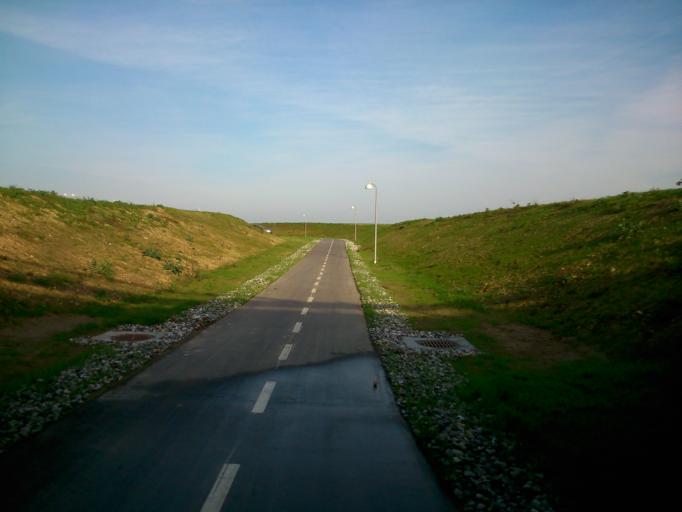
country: DK
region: South Denmark
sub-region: Middelfart Kommune
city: Strib
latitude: 55.4944
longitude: 9.8161
